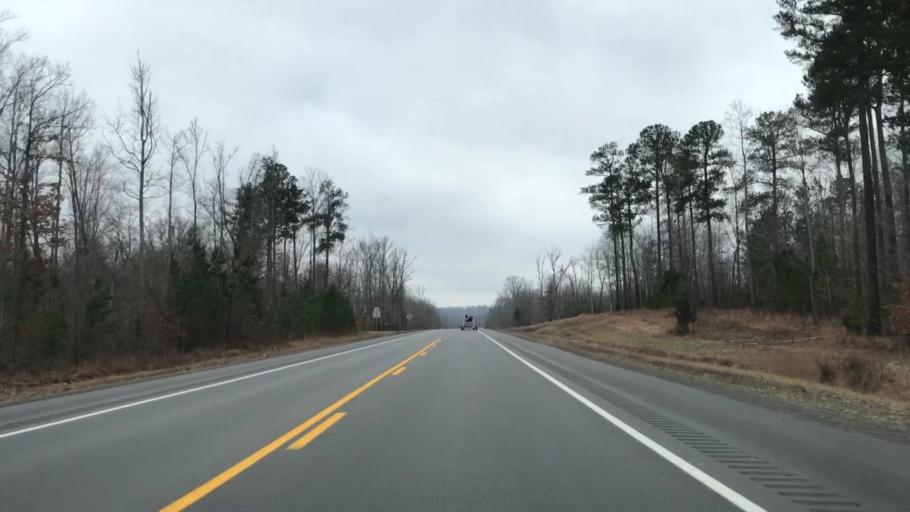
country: US
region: Kentucky
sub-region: Adair County
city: Columbia
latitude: 37.0480
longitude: -85.3645
